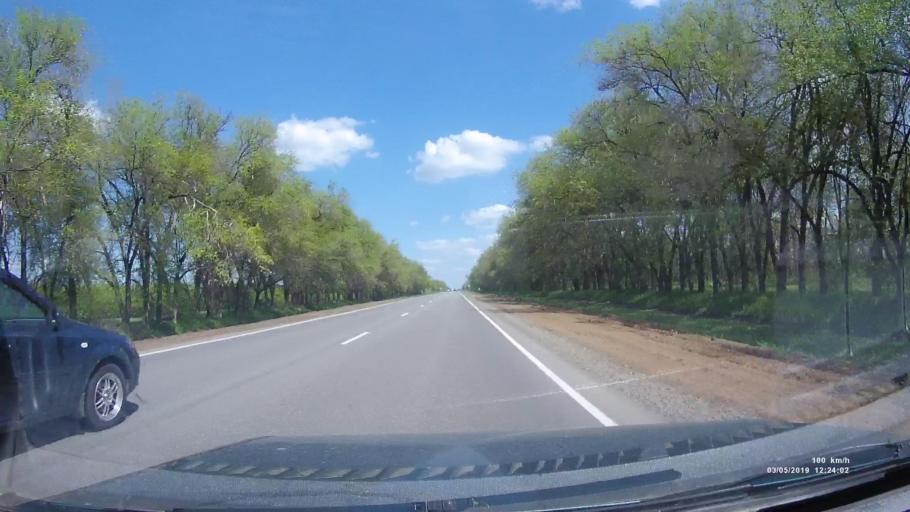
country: RU
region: Rostov
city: Semikarakorsk
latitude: 47.4156
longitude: 40.6927
